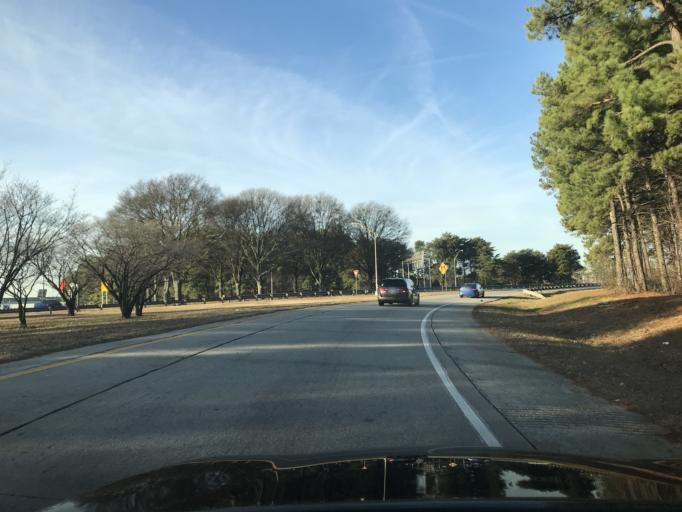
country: US
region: Georgia
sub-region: Fulton County
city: College Park
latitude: 33.6448
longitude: -84.4476
